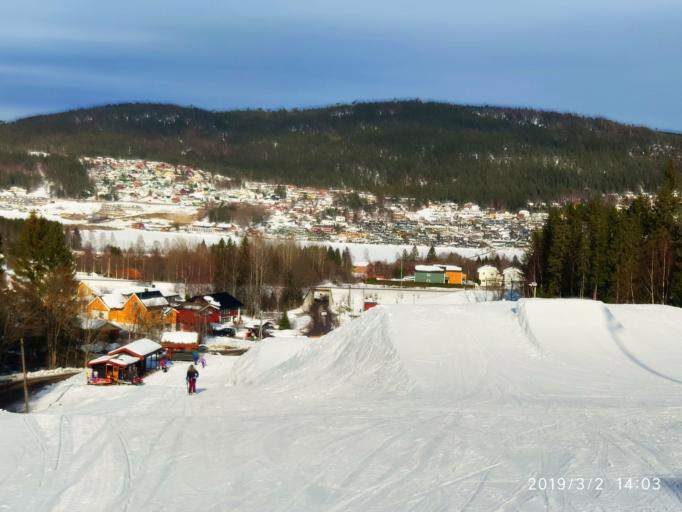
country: NO
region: Akershus
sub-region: Nittedal
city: Aneby
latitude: 60.1038
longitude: 10.8432
